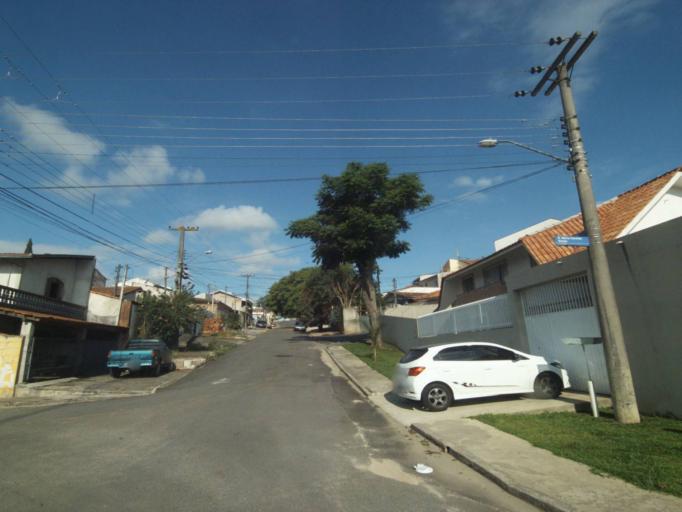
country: BR
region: Parana
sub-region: Curitiba
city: Curitiba
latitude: -25.3939
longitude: -49.3036
